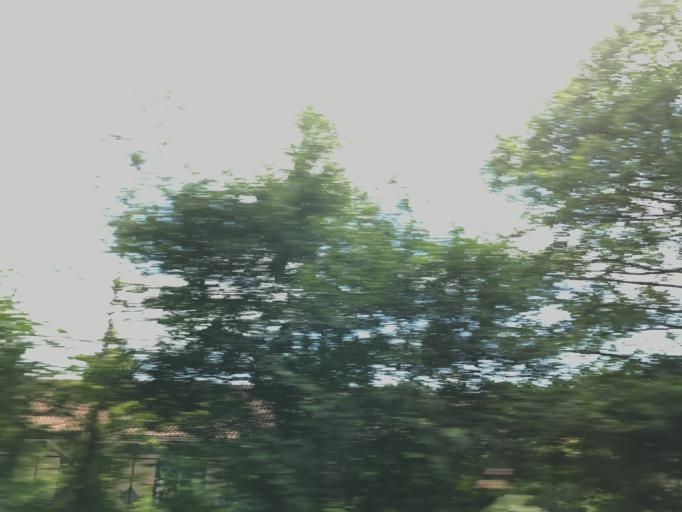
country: DE
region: Baden-Wuerttemberg
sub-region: Tuebingen Region
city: Wangen im Allgau
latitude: 47.7066
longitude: 9.8141
